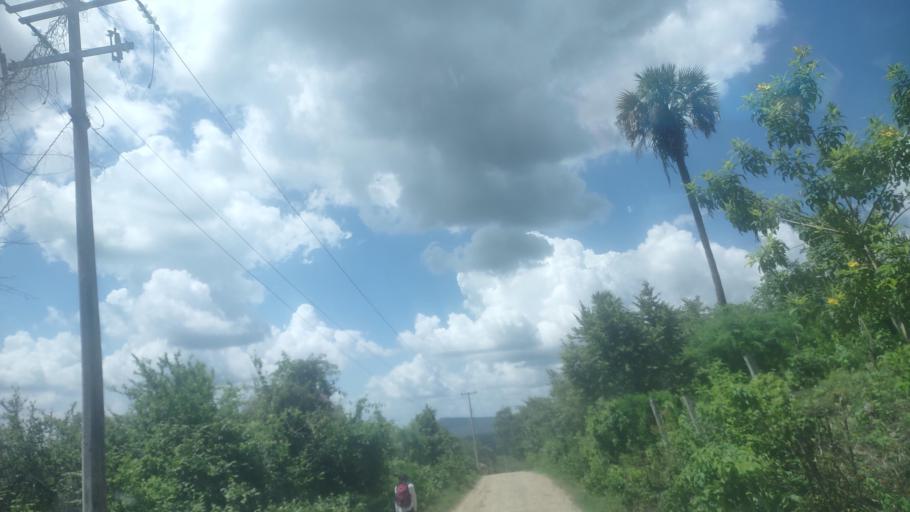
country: MX
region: Veracruz
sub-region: Tantoyuca
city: El Lindero
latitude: 21.3026
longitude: -98.1335
